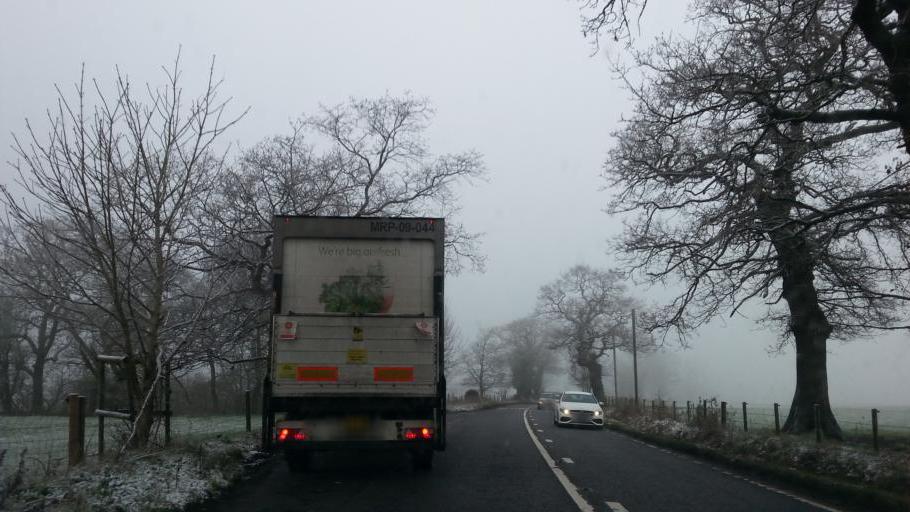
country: GB
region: England
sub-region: Cheshire East
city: Eaton
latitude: 53.1989
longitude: -2.2239
